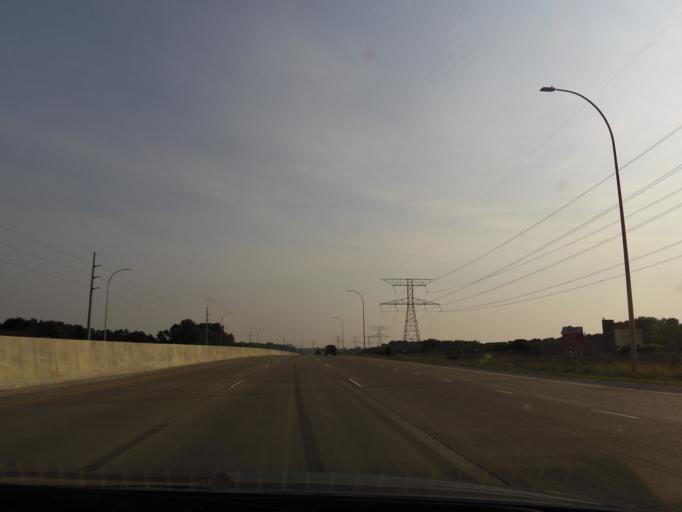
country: US
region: Minnesota
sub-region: Hennepin County
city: Plymouth
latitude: 45.0251
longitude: -93.4536
